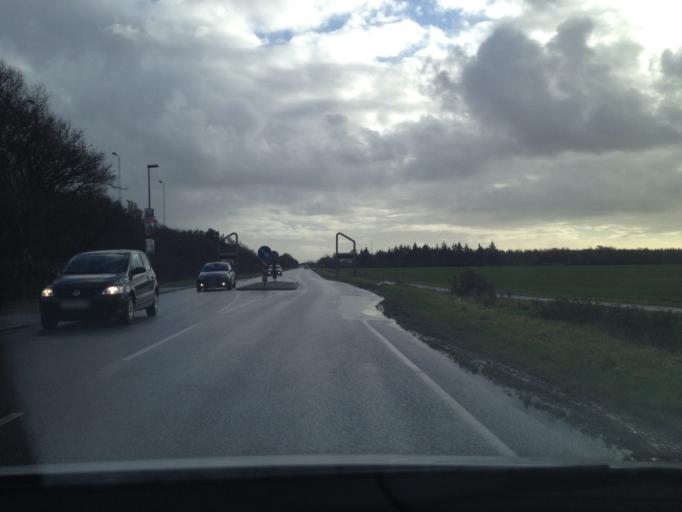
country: DK
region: South Denmark
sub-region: Tonder Kommune
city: Tonder
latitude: 54.9774
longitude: 8.8639
